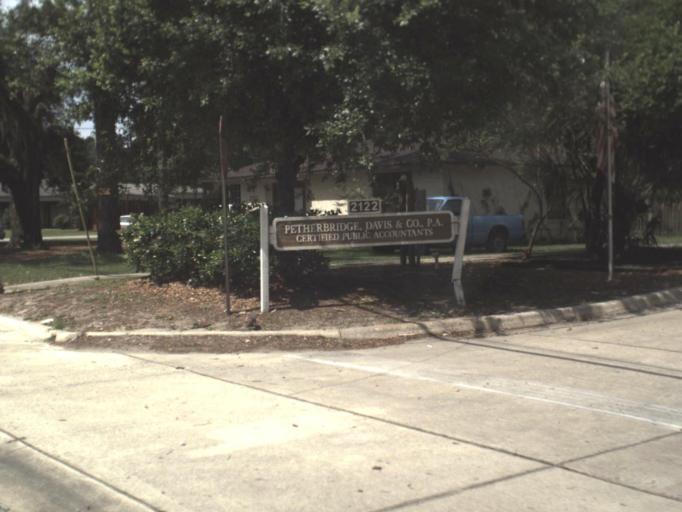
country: US
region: Florida
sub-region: Duval County
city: Jacksonville
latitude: 30.3054
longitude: -81.6007
